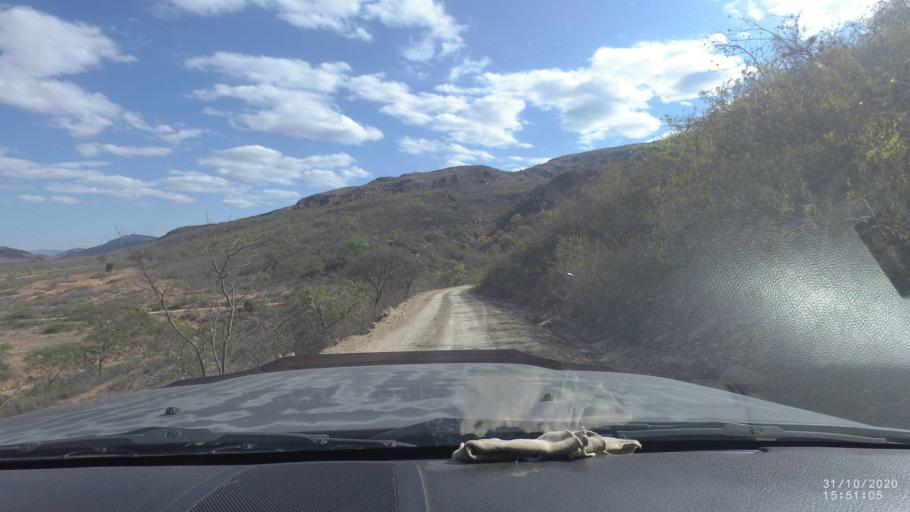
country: BO
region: Chuquisaca
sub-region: Provincia Zudanez
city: Mojocoya
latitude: -18.3150
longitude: -64.7033
